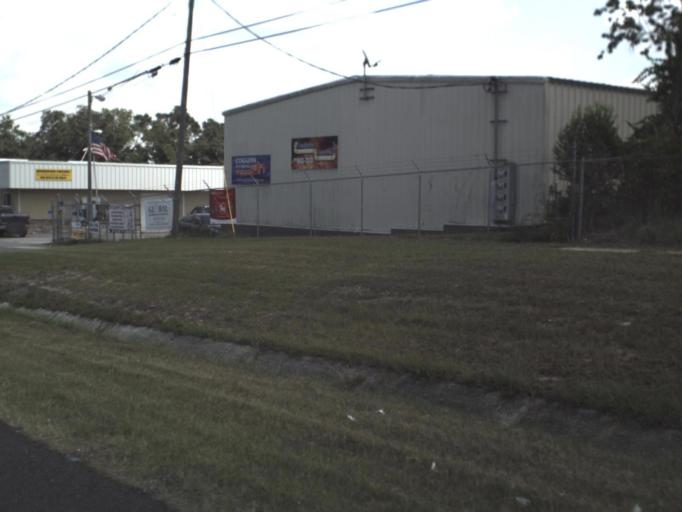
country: US
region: Florida
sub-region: Hillsborough County
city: Valrico
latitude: 27.9377
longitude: -82.2182
